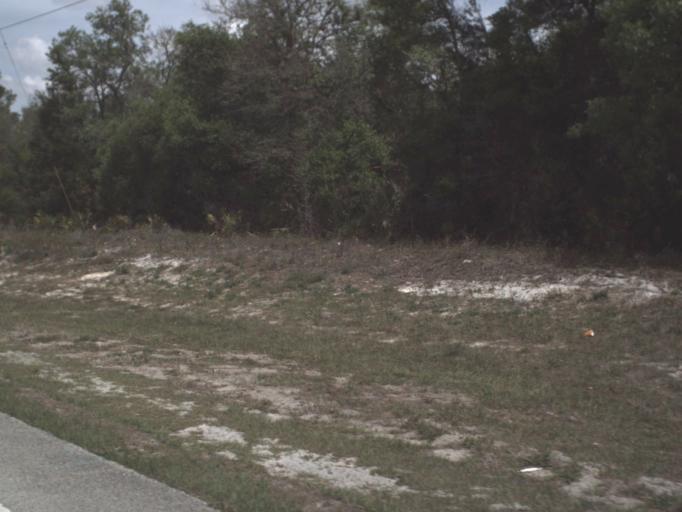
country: US
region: Florida
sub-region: Lake County
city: Lake Mack-Forest Hills
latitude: 28.9286
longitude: -81.4406
